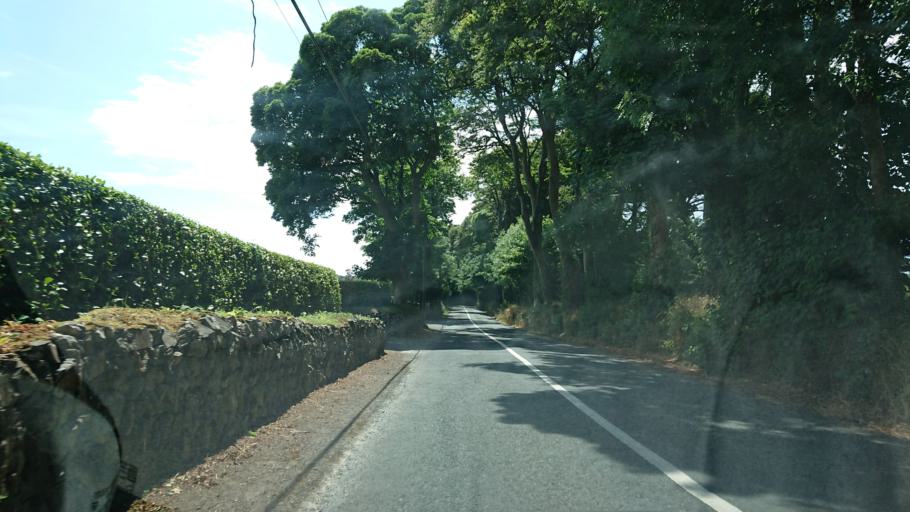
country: IE
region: Munster
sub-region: Waterford
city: Portlaw
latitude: 52.1700
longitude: -7.3350
